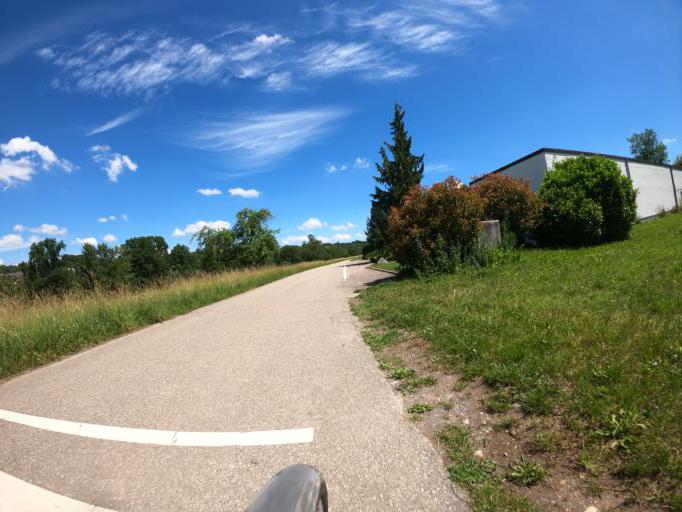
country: DE
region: Baden-Wuerttemberg
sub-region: Regierungsbezirk Stuttgart
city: Bietigheim-Bissingen
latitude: 48.9417
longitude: 9.0847
